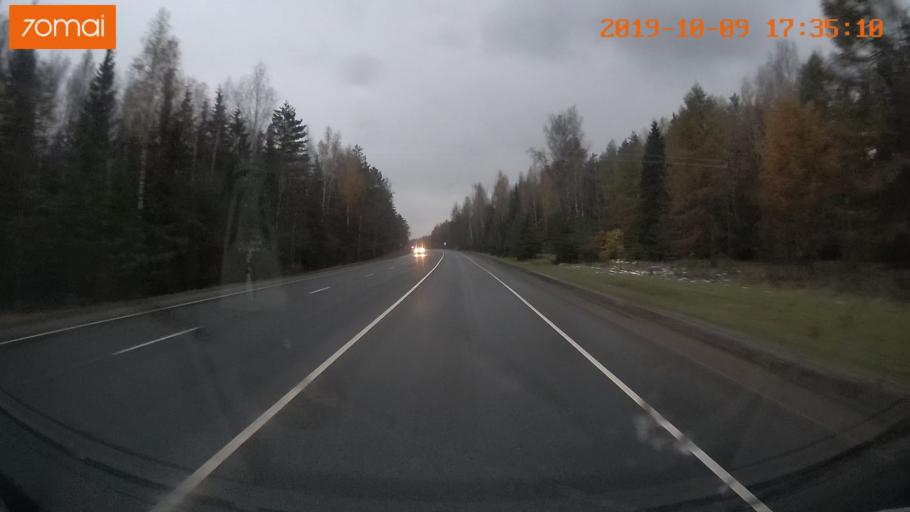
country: RU
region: Ivanovo
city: Bogorodskoye
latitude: 57.0978
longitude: 41.0042
